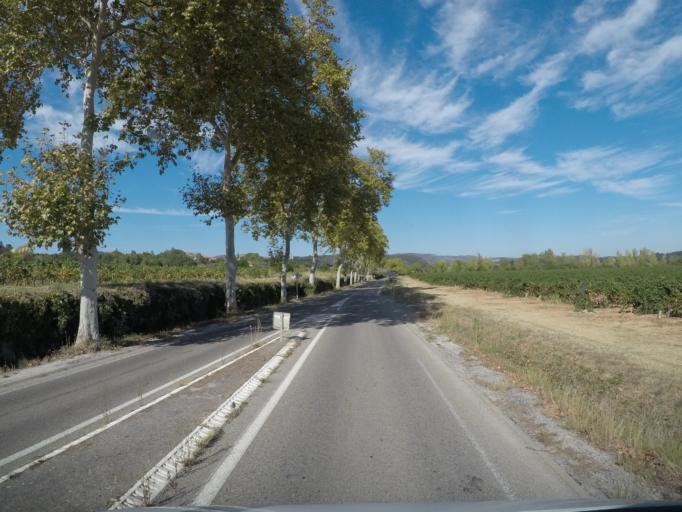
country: FR
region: Languedoc-Roussillon
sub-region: Departement du Gard
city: Boisset-et-Gaujac
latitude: 44.0253
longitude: 3.9975
